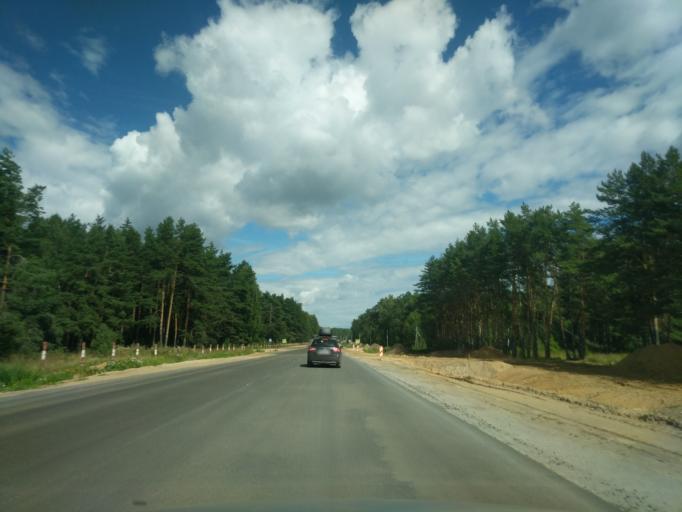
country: RU
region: Jaroslavl
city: Levashevo
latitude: 57.6661
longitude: 40.5749
